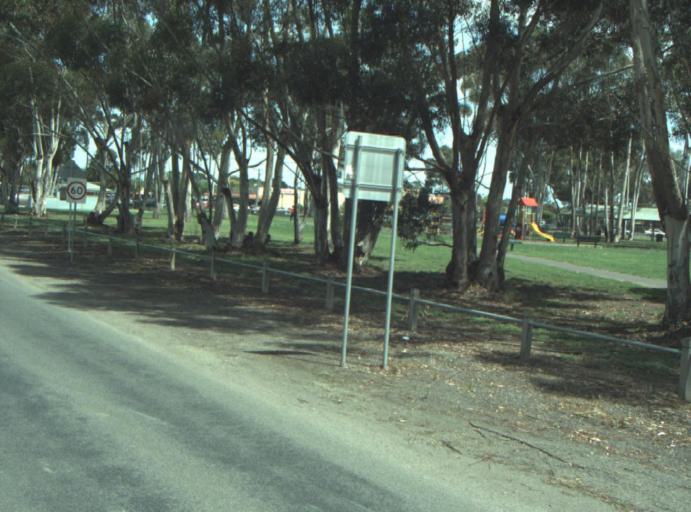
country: AU
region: Victoria
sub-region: Greater Geelong
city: Lara
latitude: -38.0230
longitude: 144.4114
